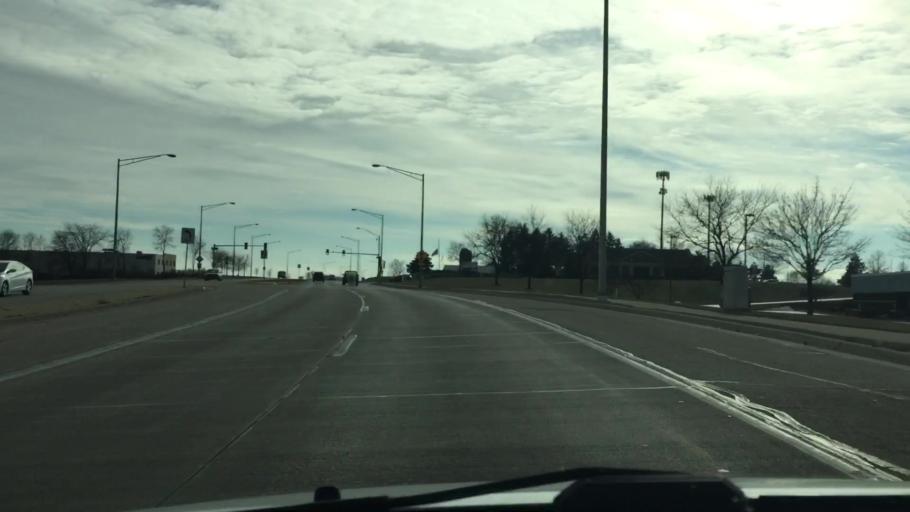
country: US
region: Illinois
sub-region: Kane County
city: Saint Charles
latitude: 41.9094
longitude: -88.2777
